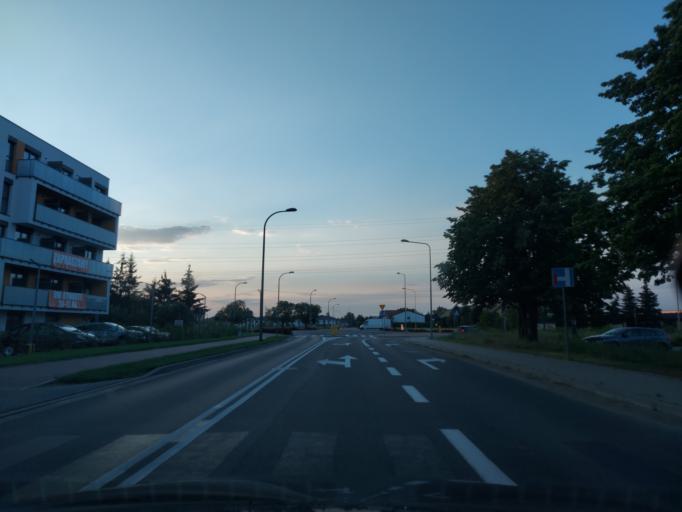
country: PL
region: Masovian Voivodeship
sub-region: Powiat piaseczynski
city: Piaseczno
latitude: 52.0873
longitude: 21.0136
